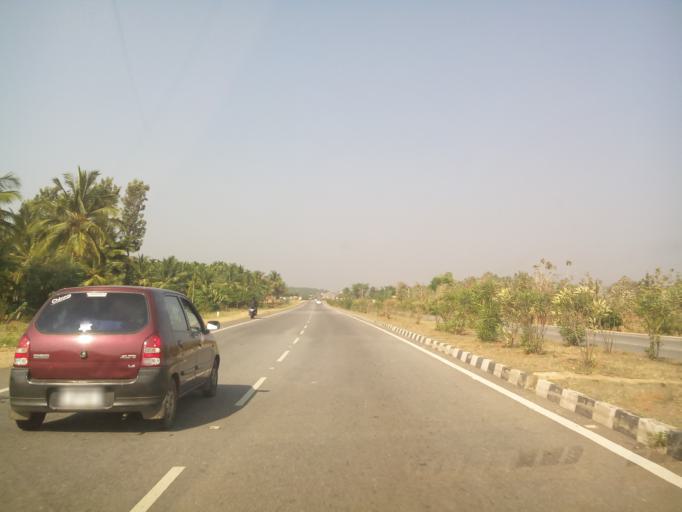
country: IN
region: Karnataka
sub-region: Tumkur
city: Kunigal
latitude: 13.0422
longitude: 77.1140
